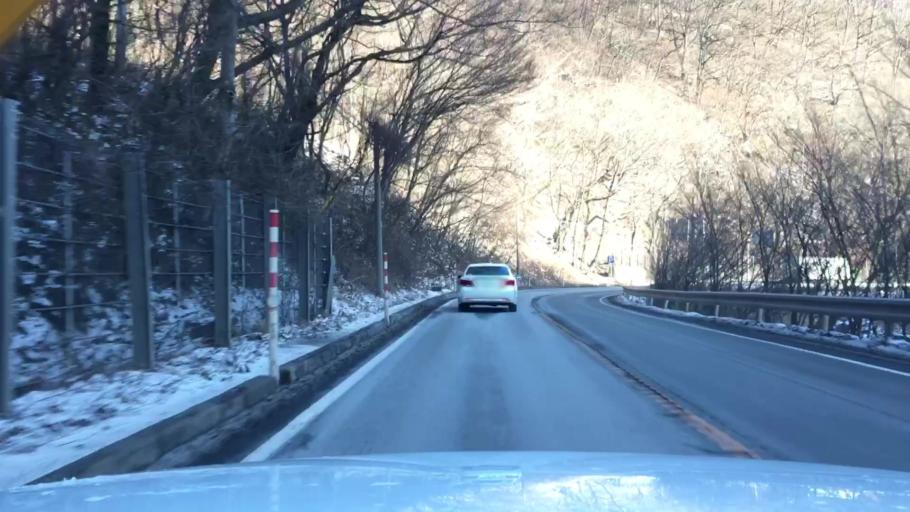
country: JP
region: Iwate
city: Tono
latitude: 39.6160
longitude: 141.4875
